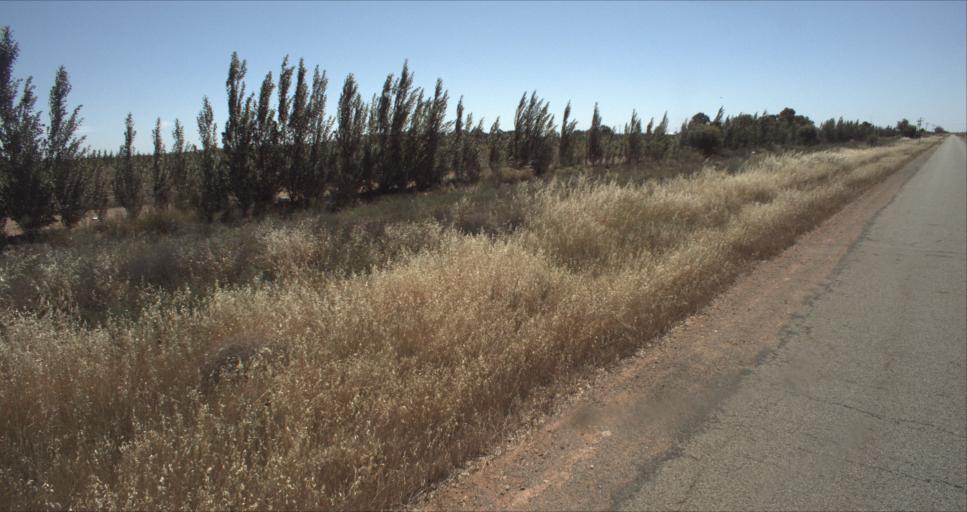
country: AU
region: New South Wales
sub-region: Leeton
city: Leeton
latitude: -34.5142
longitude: 146.3451
